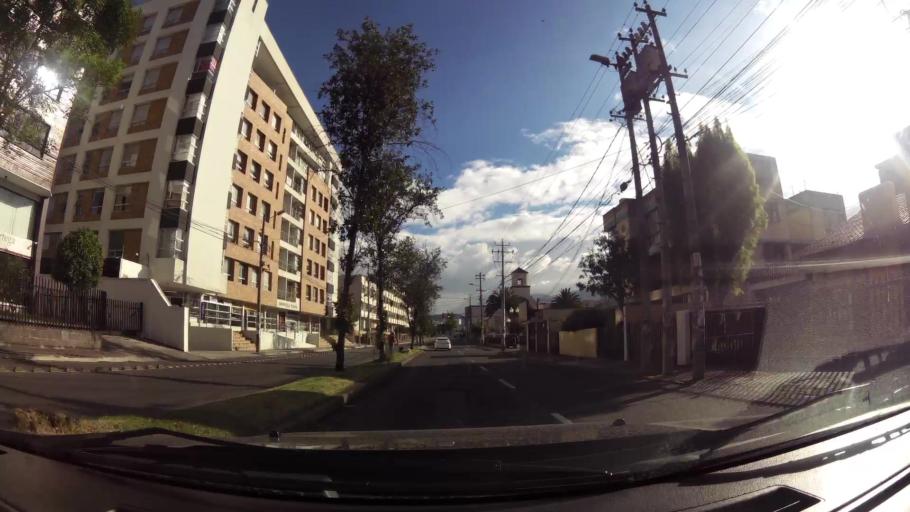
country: EC
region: Pichincha
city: Quito
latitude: -0.2070
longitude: -78.4865
